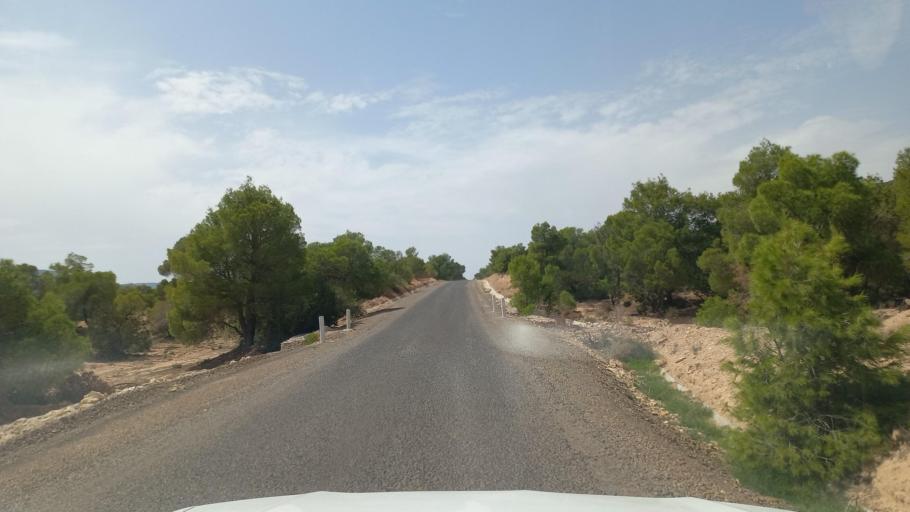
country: TN
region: Al Qasrayn
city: Sbiba
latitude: 35.3790
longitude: 8.9182
